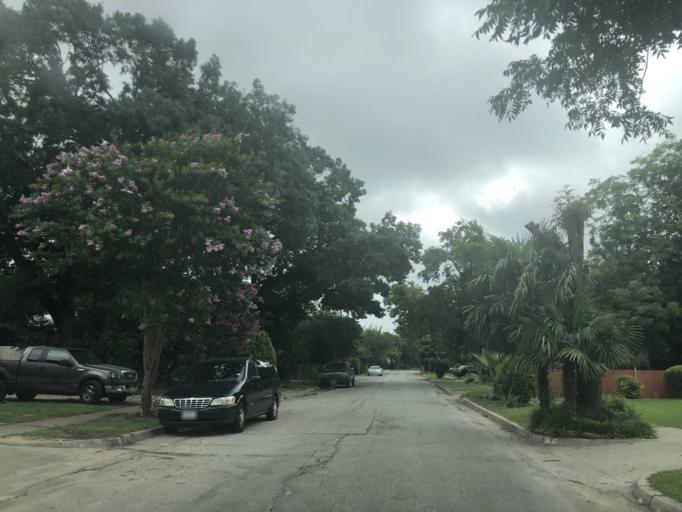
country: US
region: Texas
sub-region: Dallas County
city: University Park
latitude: 32.8674
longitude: -96.8577
